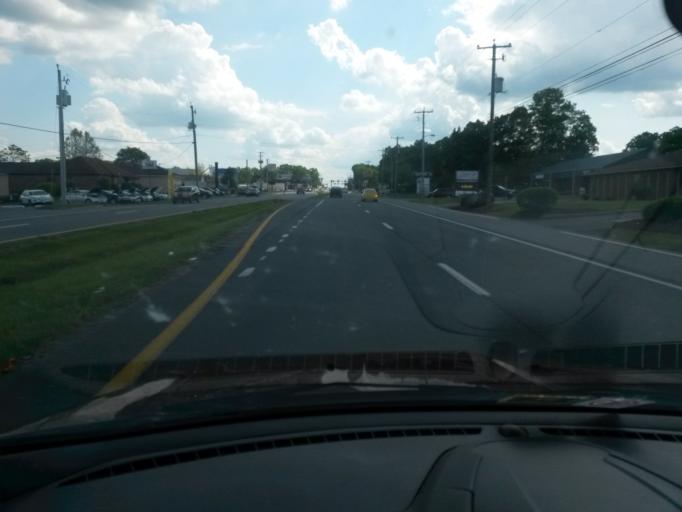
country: US
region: Virginia
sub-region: Campbell County
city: Timberlake
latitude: 37.3365
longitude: -79.2407
